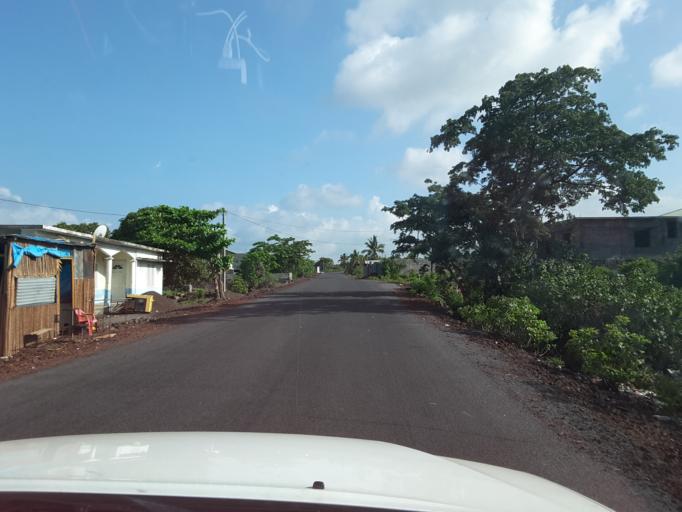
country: KM
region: Grande Comore
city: Oussivo
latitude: -11.5537
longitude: 43.2741
